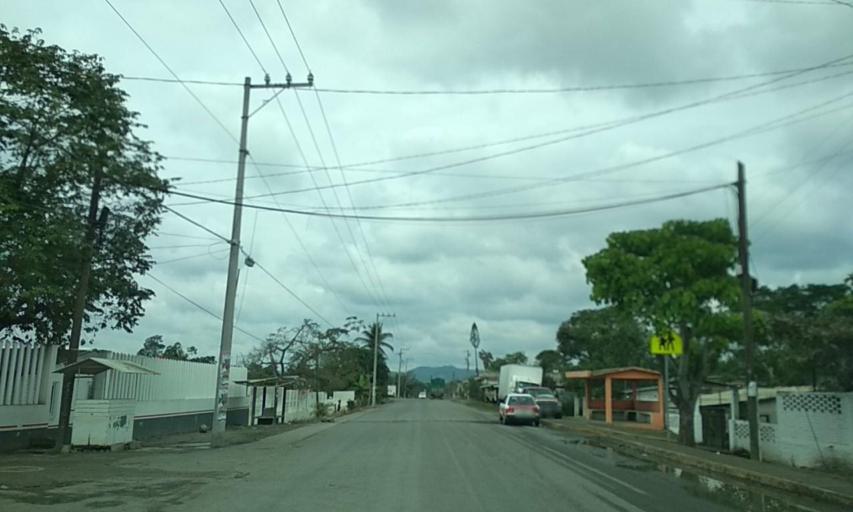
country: MX
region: Veracruz
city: Agua Dulce
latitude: 20.3630
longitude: -97.3312
